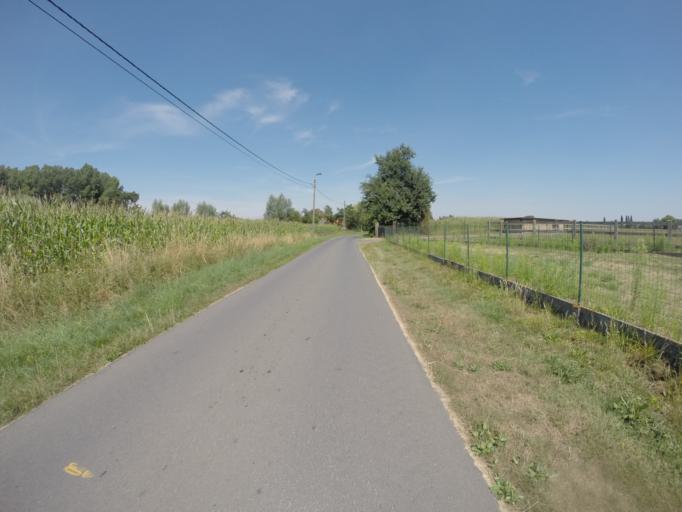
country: BE
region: Flanders
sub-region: Provincie Oost-Vlaanderen
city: Knesselare
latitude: 51.1299
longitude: 3.4004
